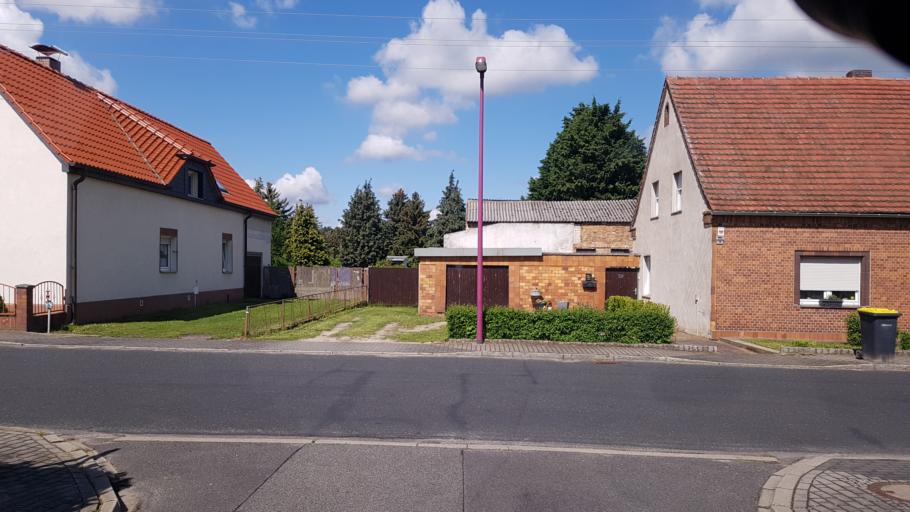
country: DE
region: Brandenburg
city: Sallgast
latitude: 51.5905
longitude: 13.9233
